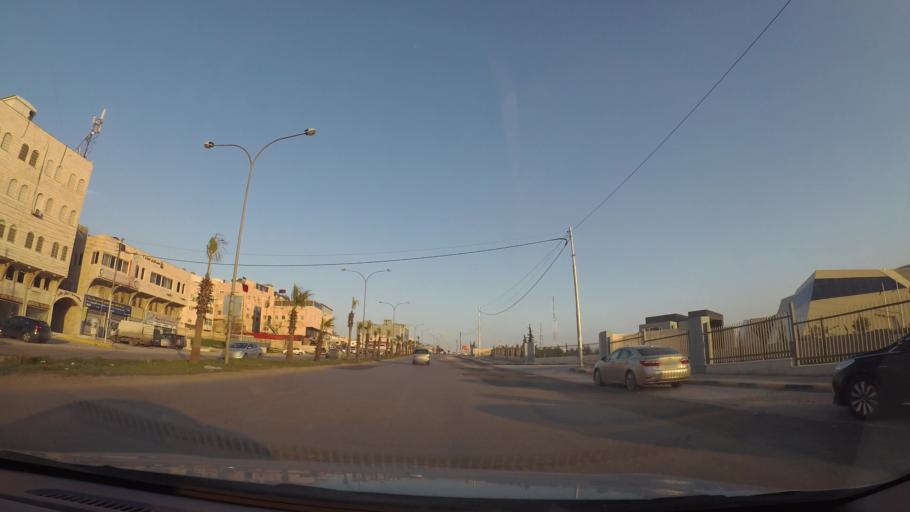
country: JO
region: Amman
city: Al Quwaysimah
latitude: 31.9104
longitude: 35.9248
